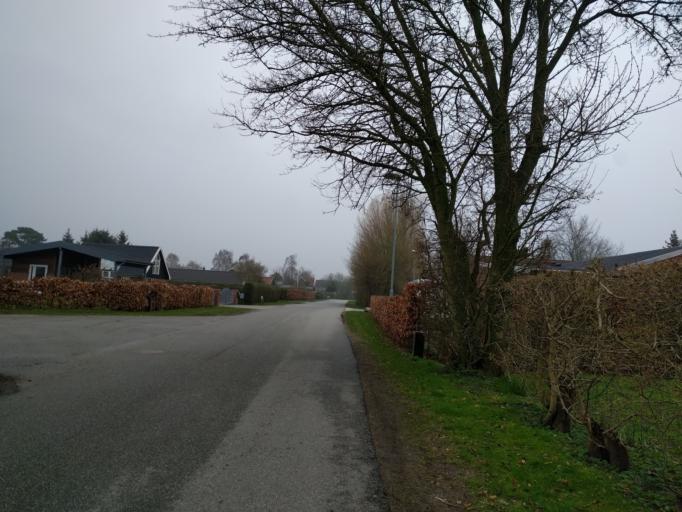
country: DK
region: Central Jutland
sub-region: Arhus Kommune
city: Lystrup
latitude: 56.2094
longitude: 10.2410
